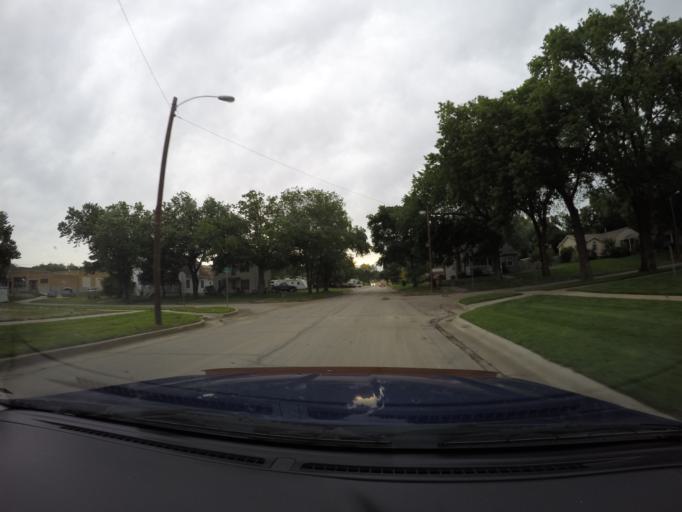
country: US
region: Kansas
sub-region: Clay County
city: Clay Center
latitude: 39.3780
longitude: -97.1192
